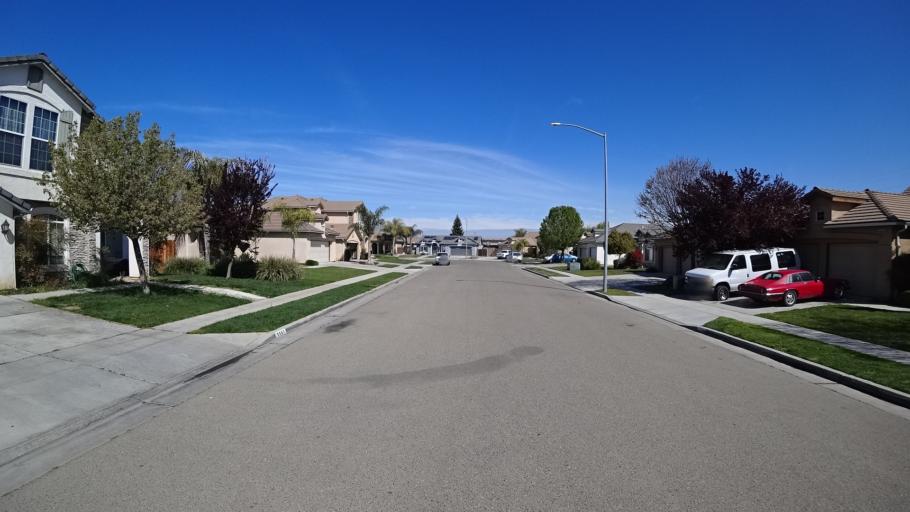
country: US
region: California
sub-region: Fresno County
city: Biola
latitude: 36.8167
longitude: -119.9028
